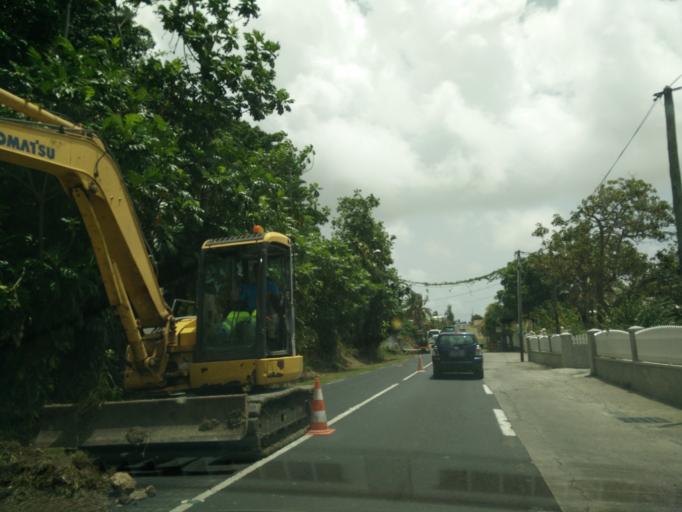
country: GP
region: Guadeloupe
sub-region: Guadeloupe
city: Petit-Canal
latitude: 16.3566
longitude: -61.4559
